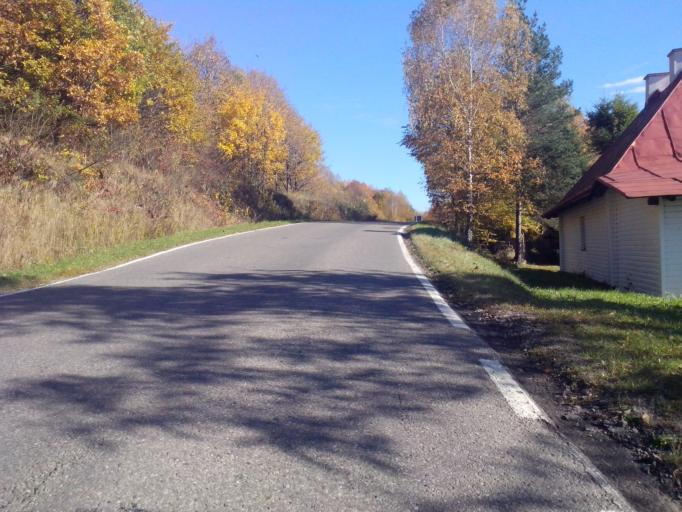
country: PL
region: Subcarpathian Voivodeship
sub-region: Powiat krosnienski
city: Korczyna
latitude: 49.7671
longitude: 21.8062
